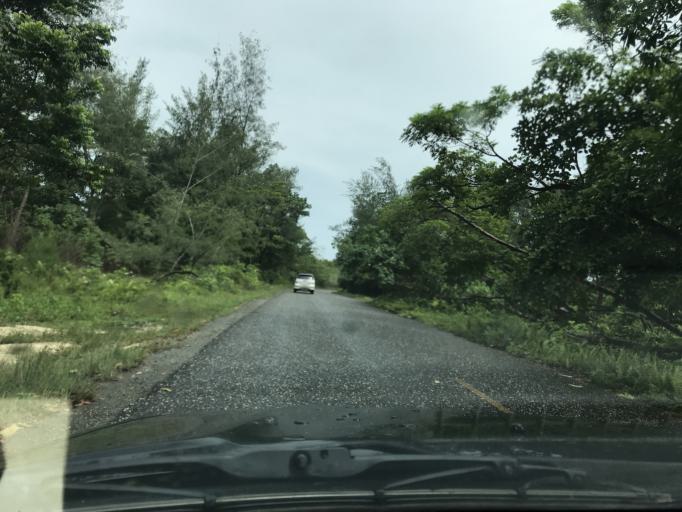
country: SB
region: Western Province
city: Gizo
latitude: -8.3250
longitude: 157.2580
